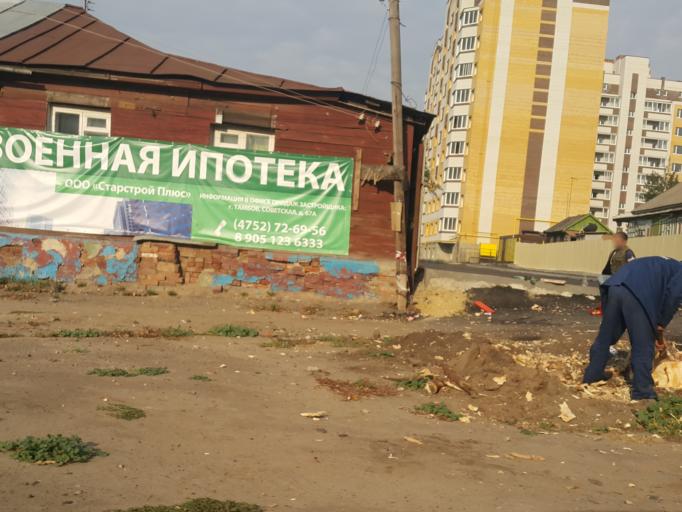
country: RU
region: Tambov
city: Tambov
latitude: 52.7023
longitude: 41.4649
